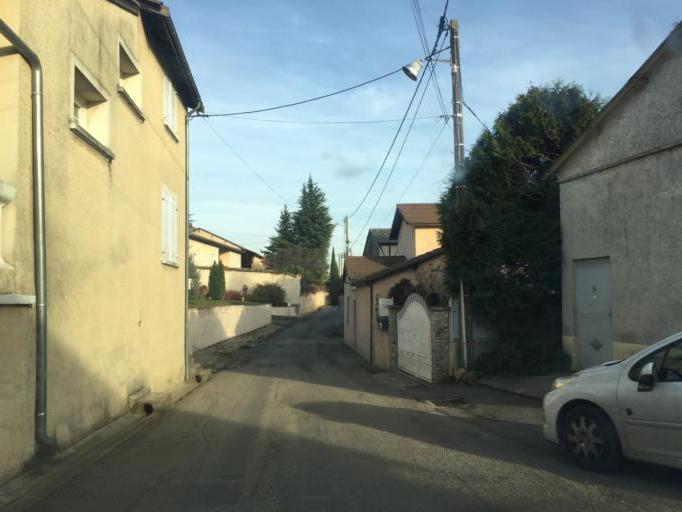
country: FR
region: Rhone-Alpes
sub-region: Departement de l'Ain
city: Miribel
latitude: 45.8302
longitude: 4.9478
